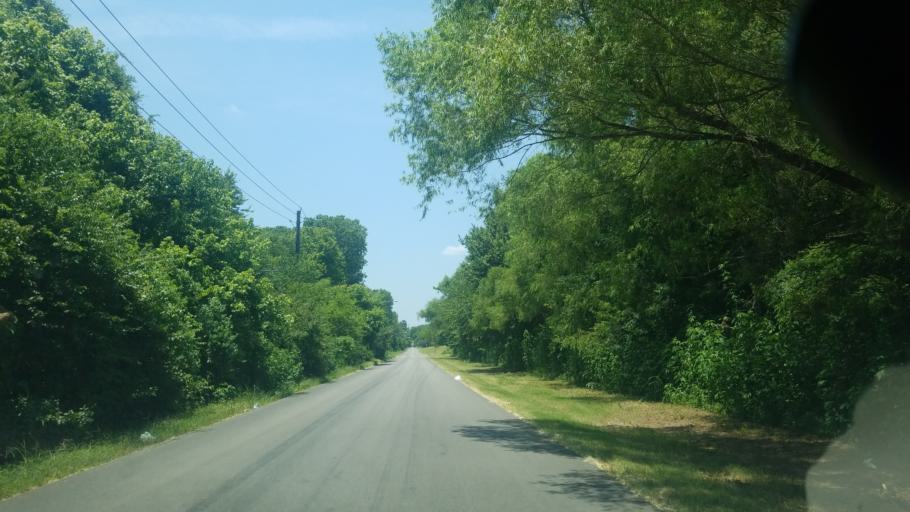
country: US
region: Texas
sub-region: Dallas County
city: Dallas
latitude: 32.7321
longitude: -96.7798
